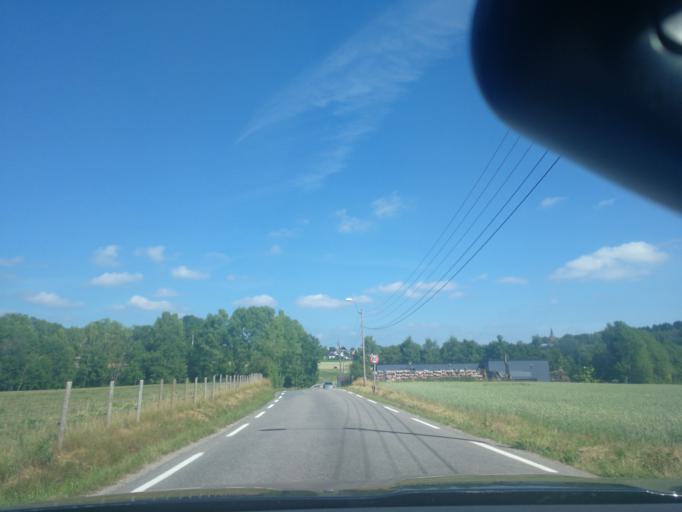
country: NO
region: Vestfold
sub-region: Stokke
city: Stokke
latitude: 59.2123
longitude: 10.2938
